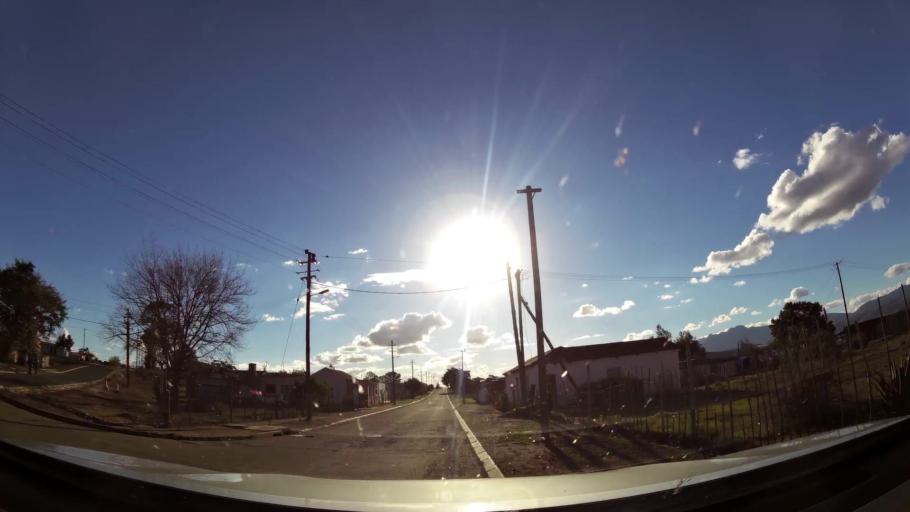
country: ZA
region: Western Cape
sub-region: Eden District Municipality
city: Riversdale
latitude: -34.1015
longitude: 20.9665
